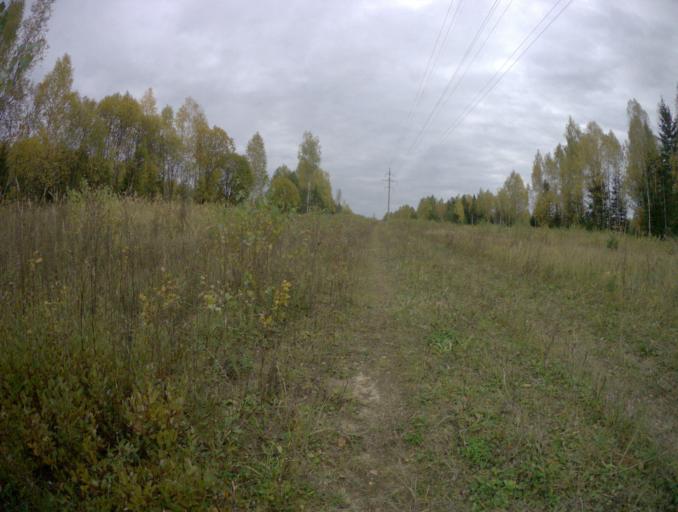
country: RU
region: Vladimir
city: Stepantsevo
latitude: 56.3052
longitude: 41.7498
